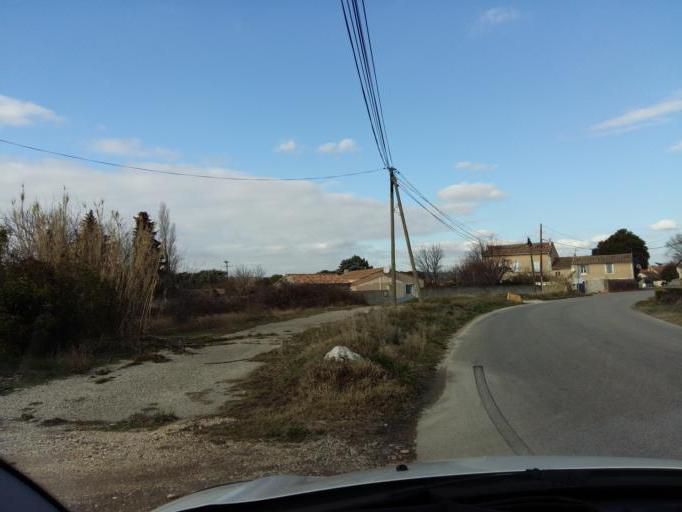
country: FR
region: Provence-Alpes-Cote d'Azur
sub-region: Departement du Vaucluse
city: Cheval-Blanc
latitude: 43.8062
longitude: 5.0511
